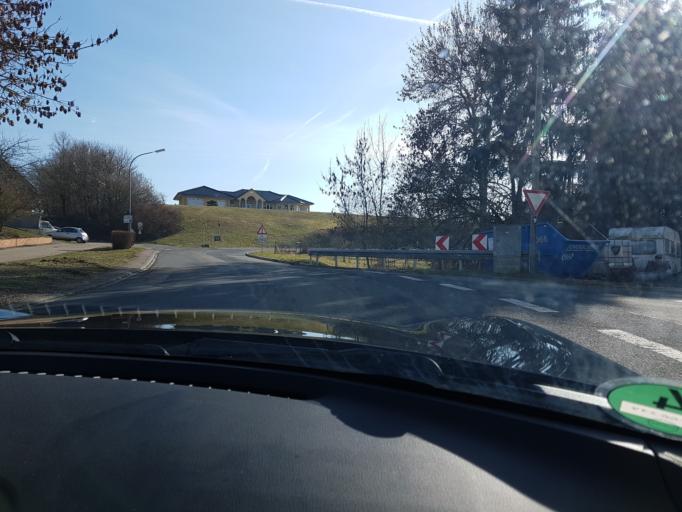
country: DE
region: Baden-Wuerttemberg
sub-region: Regierungsbezirk Stuttgart
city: Krautheim
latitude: 49.4079
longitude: 9.6132
